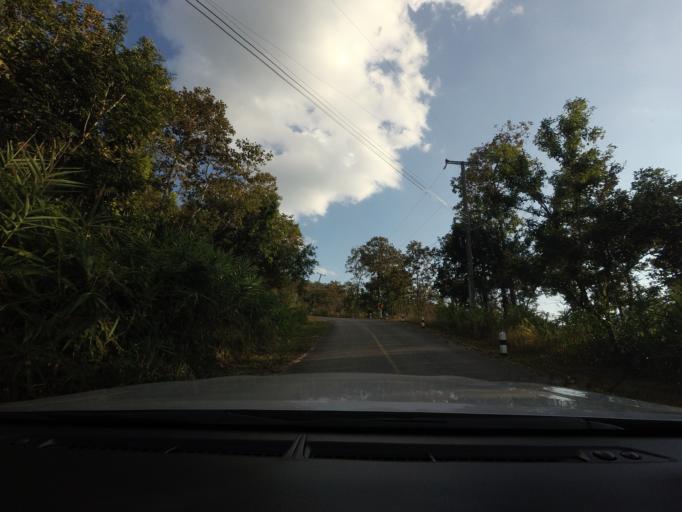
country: TH
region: Chiang Mai
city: Phrao
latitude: 19.4916
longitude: 99.1664
